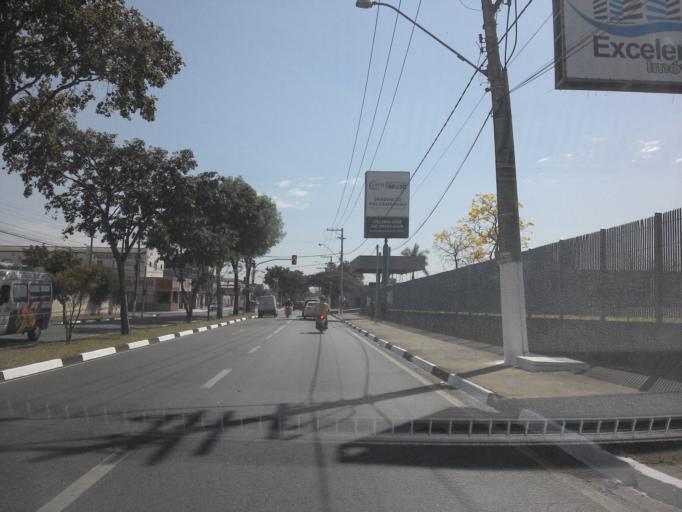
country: BR
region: Sao Paulo
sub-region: Hortolandia
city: Hortolandia
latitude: -22.8943
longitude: -47.2303
